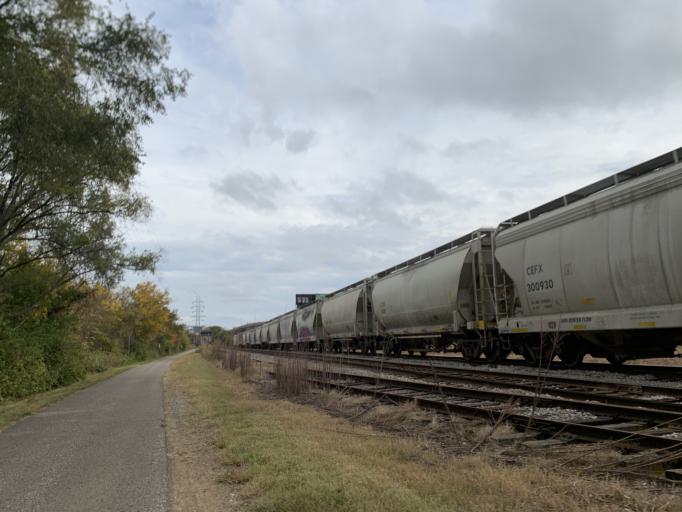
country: US
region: Kentucky
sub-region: Jefferson County
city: Louisville
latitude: 38.2665
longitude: -85.7756
